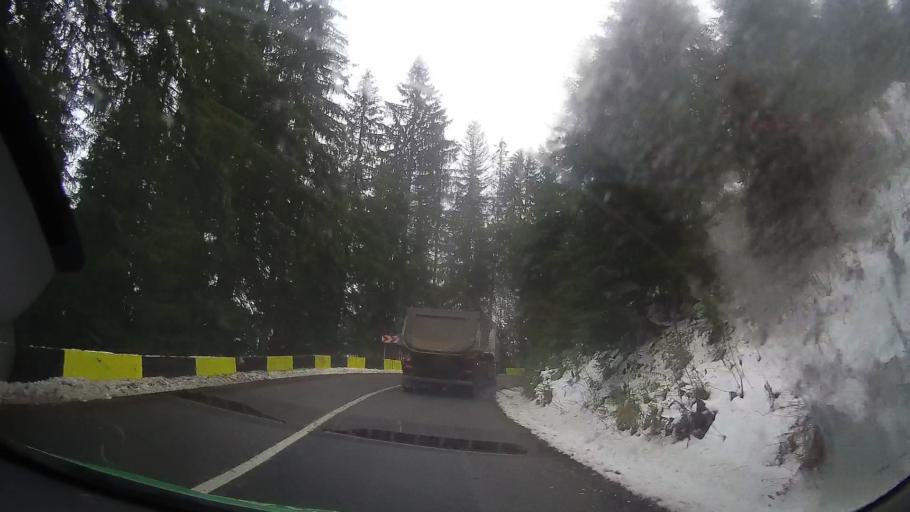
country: RO
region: Harghita
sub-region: Oras Balan
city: Balan
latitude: 46.7777
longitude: 25.7434
